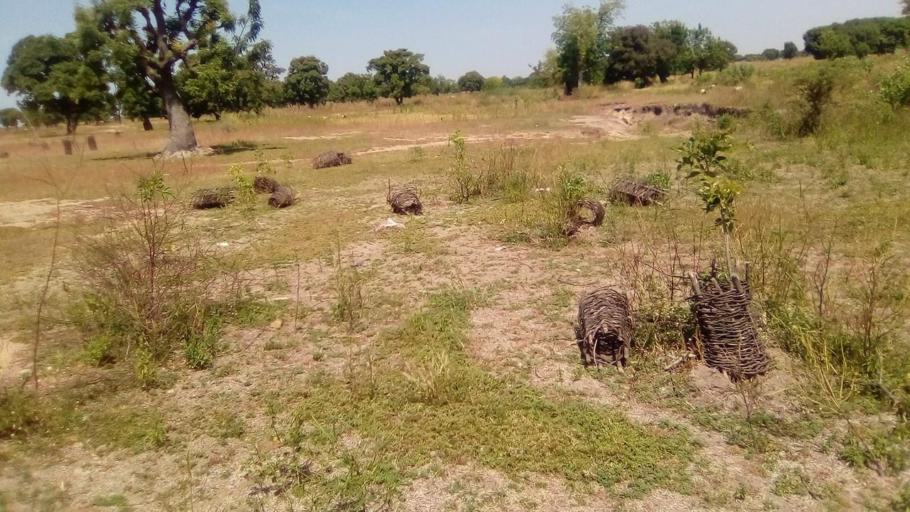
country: GH
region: Upper East
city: Bawku
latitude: 11.0941
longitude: -0.0720
